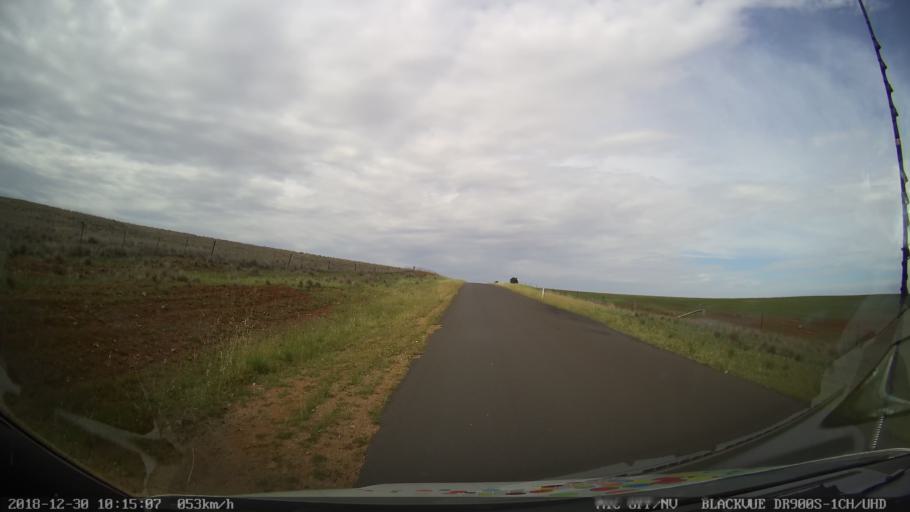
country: AU
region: New South Wales
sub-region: Snowy River
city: Berridale
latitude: -36.5412
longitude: 149.0480
